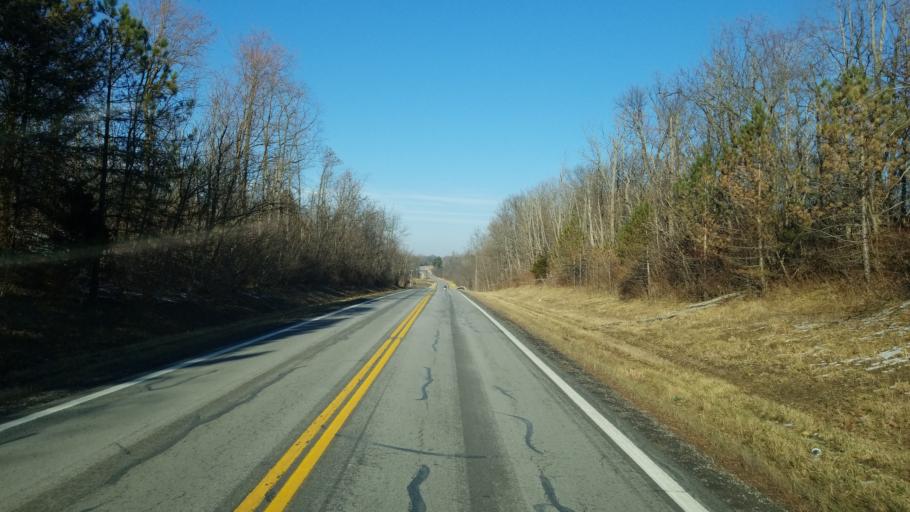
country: US
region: Ohio
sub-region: Huron County
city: Willard
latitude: 41.0915
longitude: -82.6615
